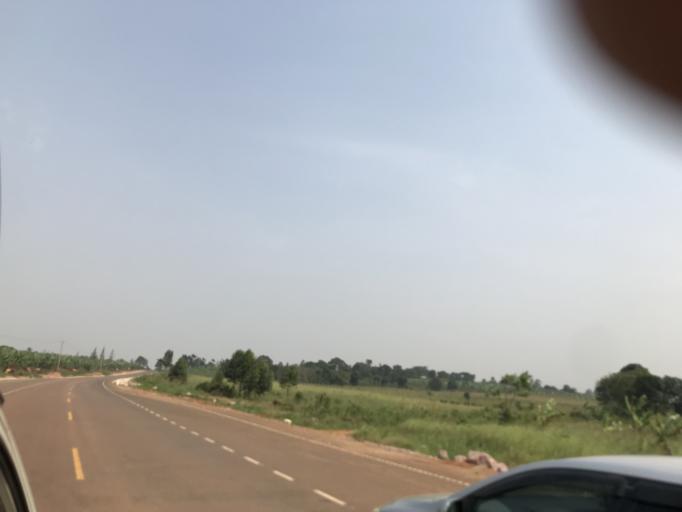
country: UG
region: Central Region
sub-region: Kalungu District
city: Kalungu
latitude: -0.2278
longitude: 31.7296
